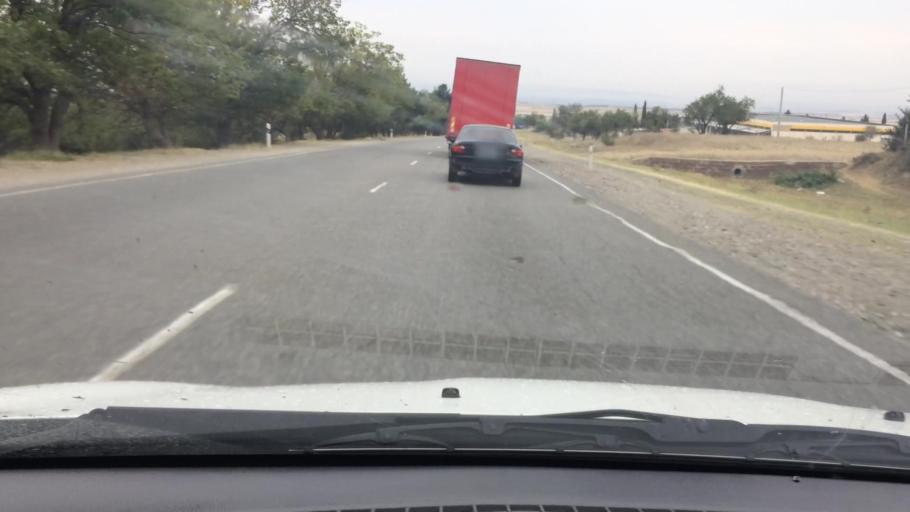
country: GE
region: T'bilisi
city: Tbilisi
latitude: 41.6408
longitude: 44.8640
